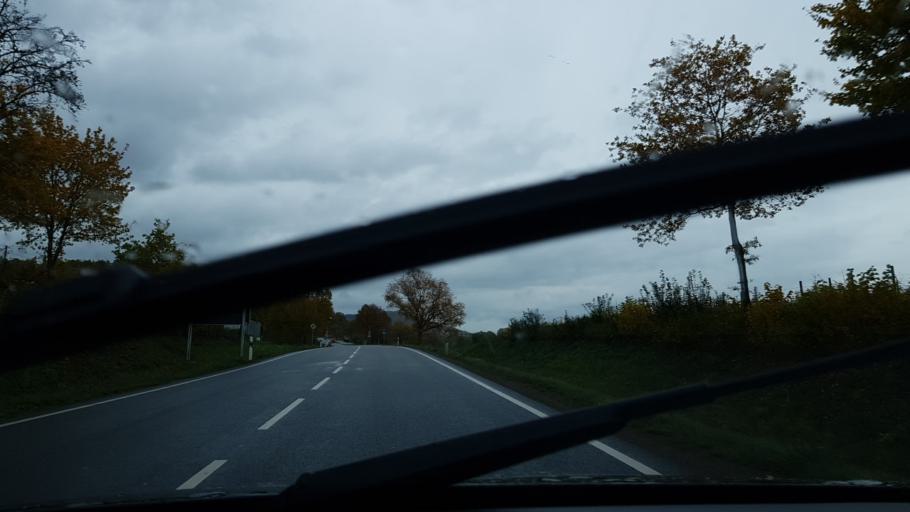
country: DE
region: Rheinland-Pfalz
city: Sehlem
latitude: 49.9043
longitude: 6.8269
